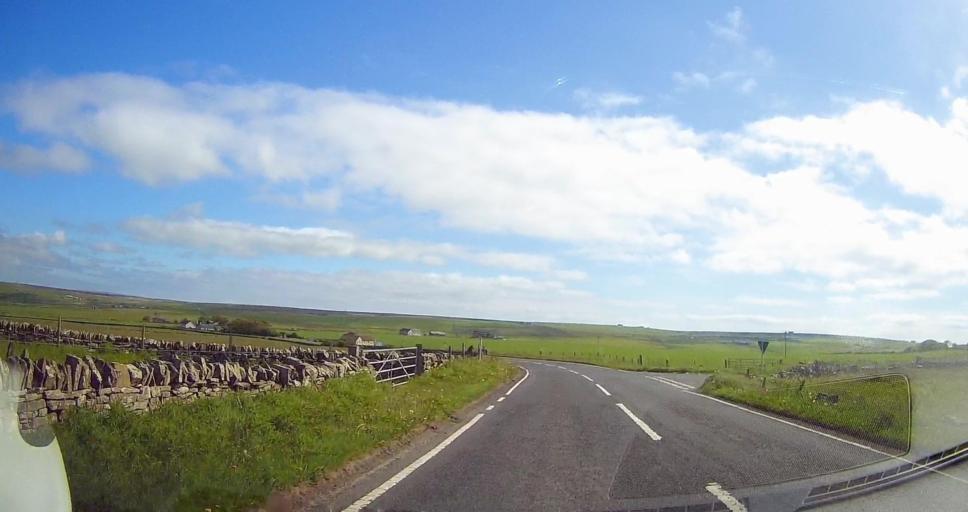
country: GB
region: Scotland
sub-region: Orkney Islands
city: Kirkwall
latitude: 58.9647
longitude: -2.9413
